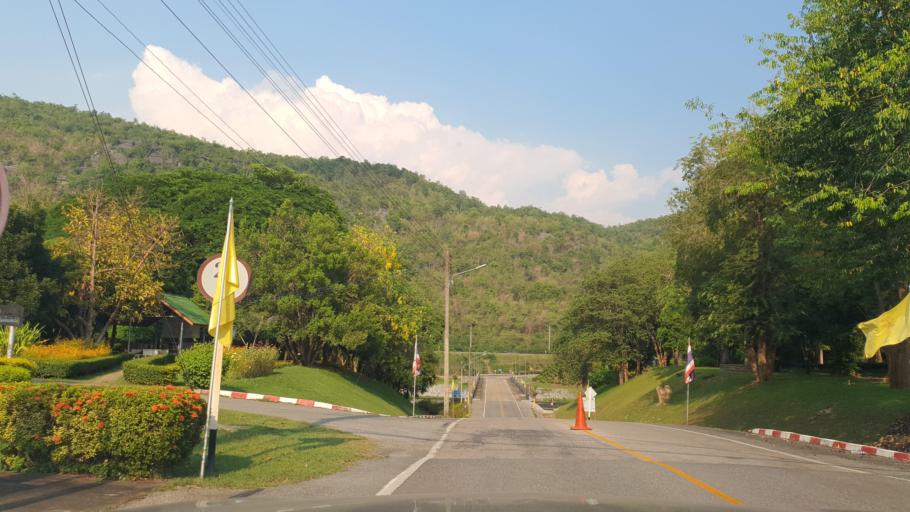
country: TH
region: Kanchanaburi
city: Sai Yok
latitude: 14.2298
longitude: 99.2366
